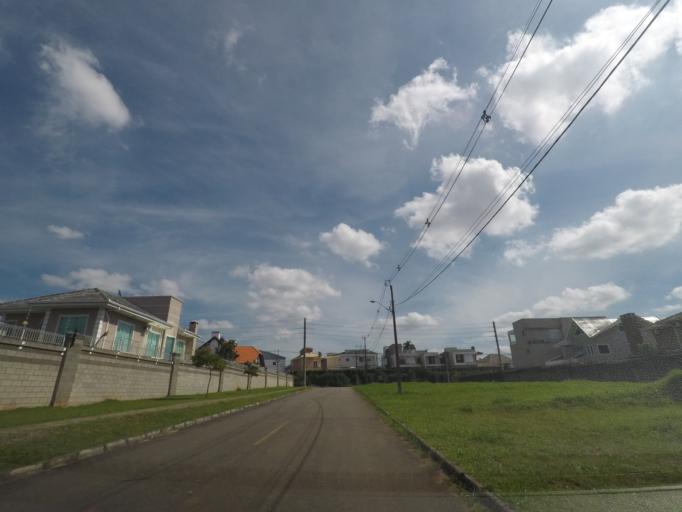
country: BR
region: Parana
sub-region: Curitiba
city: Curitiba
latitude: -25.4943
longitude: -49.2677
